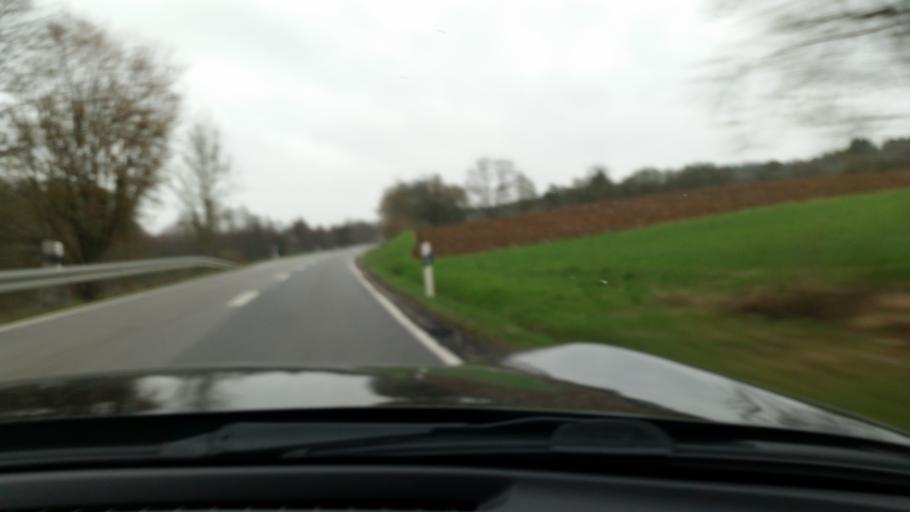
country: DE
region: Baden-Wuerttemberg
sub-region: Karlsruhe Region
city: Osterburken
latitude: 49.4650
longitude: 9.4160
